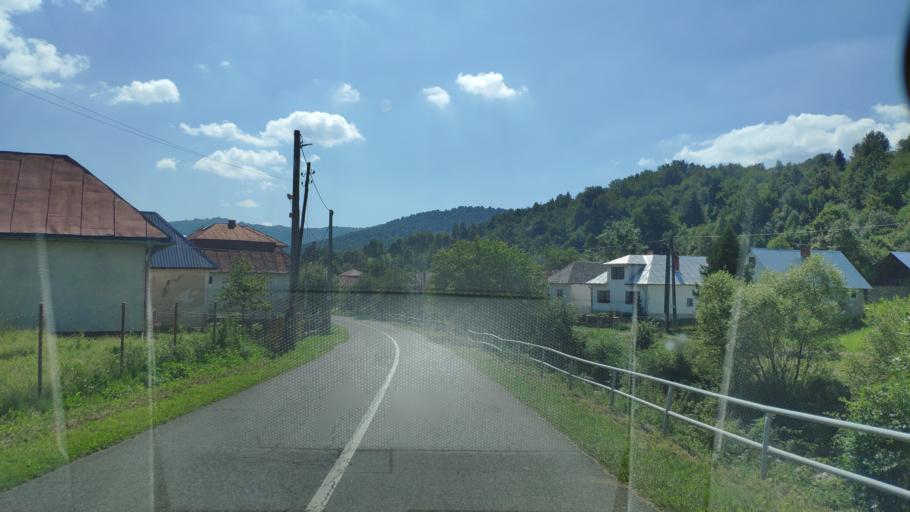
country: PL
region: Subcarpathian Voivodeship
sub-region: Powiat leski
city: Cisna
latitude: 49.0520
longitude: 22.3550
